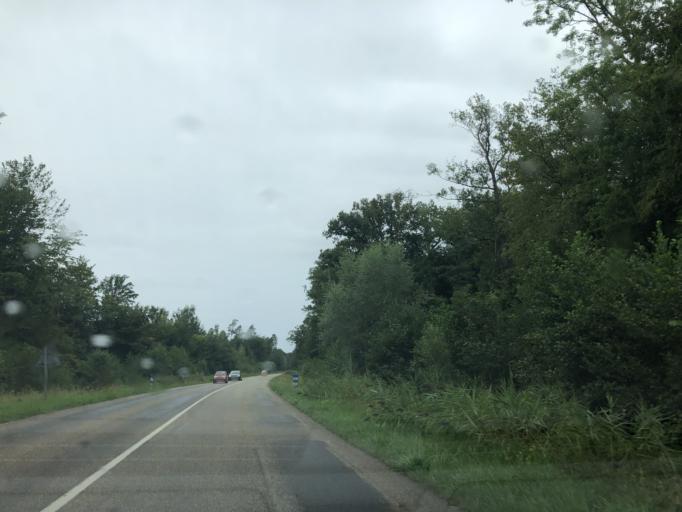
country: DE
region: Rheinland-Pfalz
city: Scheibenhardt
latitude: 48.9887
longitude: 8.0849
